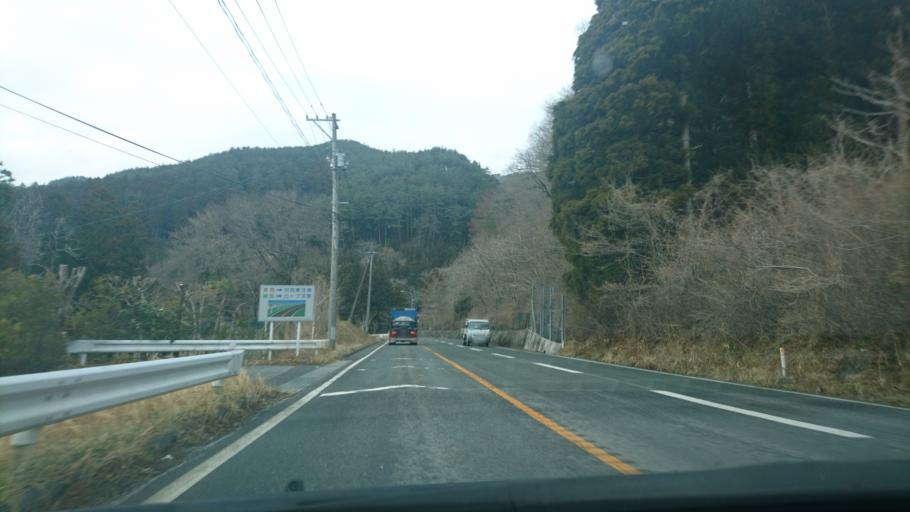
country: JP
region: Iwate
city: Ofunato
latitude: 39.0271
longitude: 141.6831
